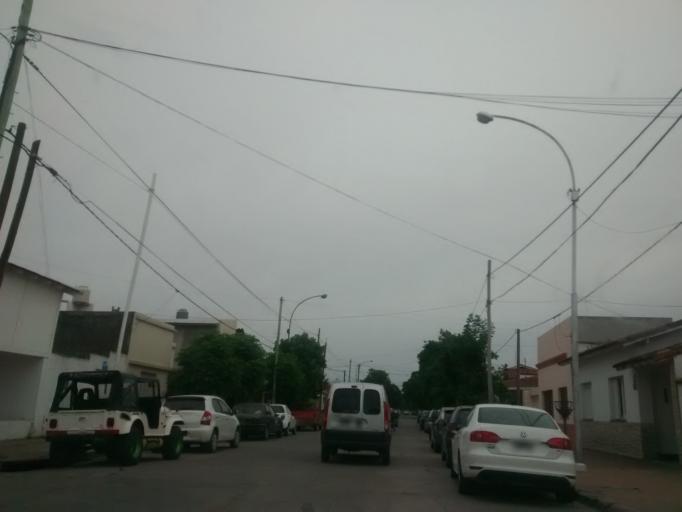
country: AR
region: Buenos Aires
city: Necochea
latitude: -38.5597
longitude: -58.7304
